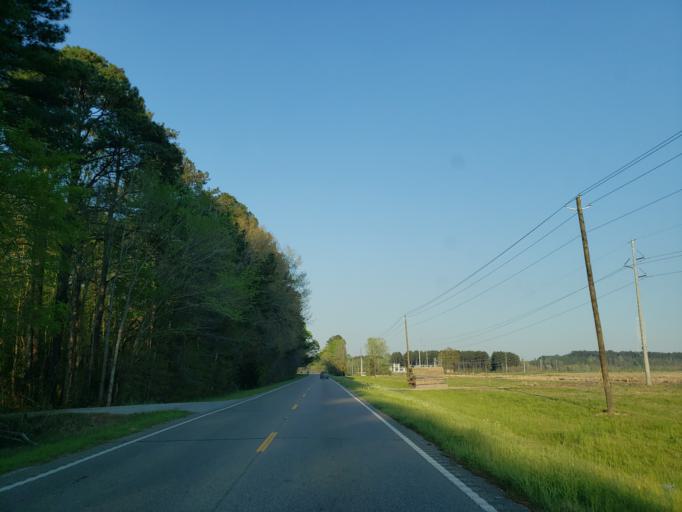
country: US
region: Mississippi
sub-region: Lauderdale County
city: Marion
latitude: 32.3949
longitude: -88.6232
